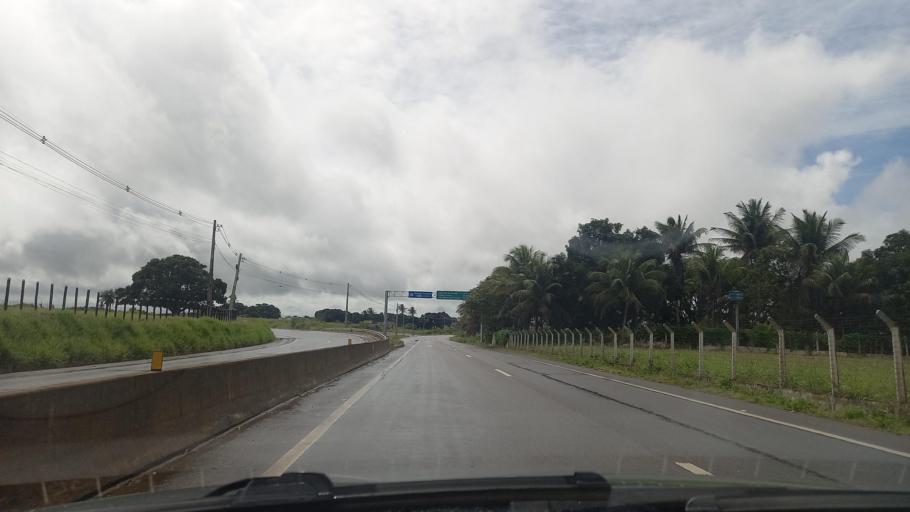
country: BR
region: Alagoas
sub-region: Limoeiro De Anadia
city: Limoeiro de Anadia
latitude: -9.7607
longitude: -36.5701
